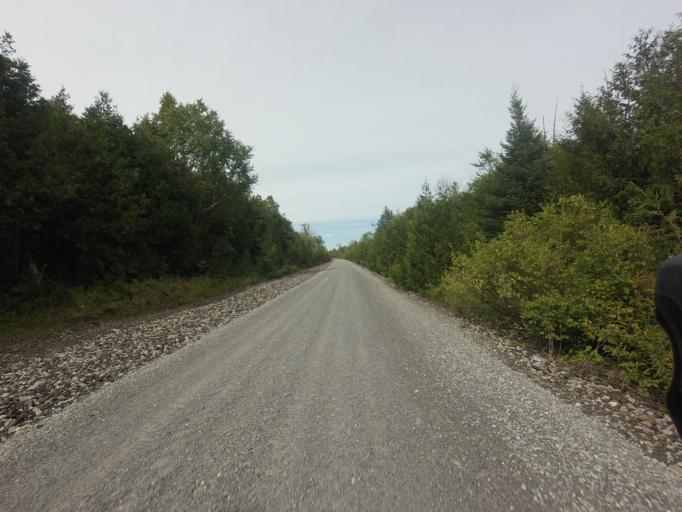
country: CA
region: Ontario
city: Carleton Place
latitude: 45.1175
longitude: -76.1254
